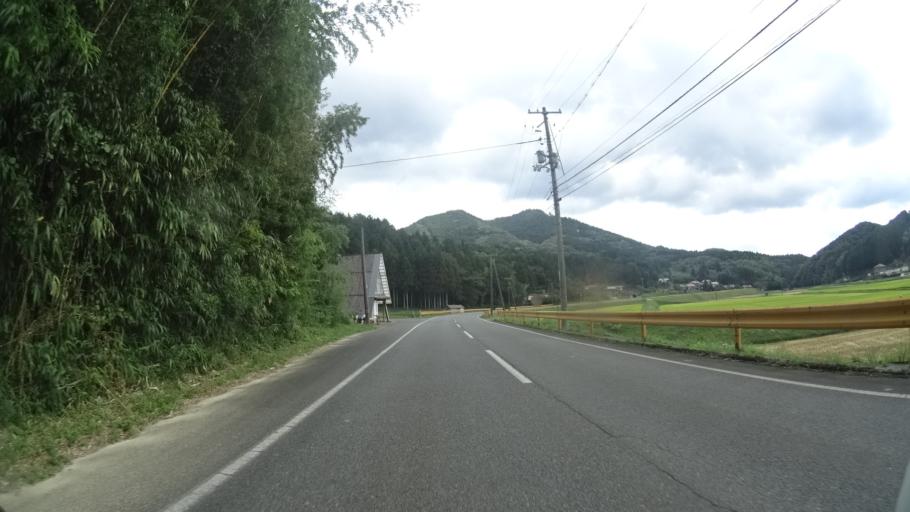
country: JP
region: Yamaguchi
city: Hagi
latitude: 34.5293
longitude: 131.6047
